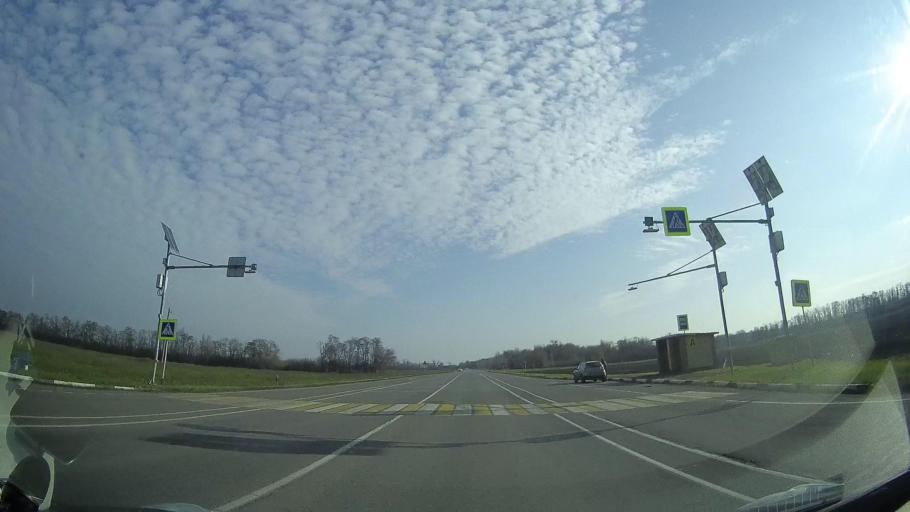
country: RU
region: Rostov
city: Gigant
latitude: 46.5303
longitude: 41.1884
